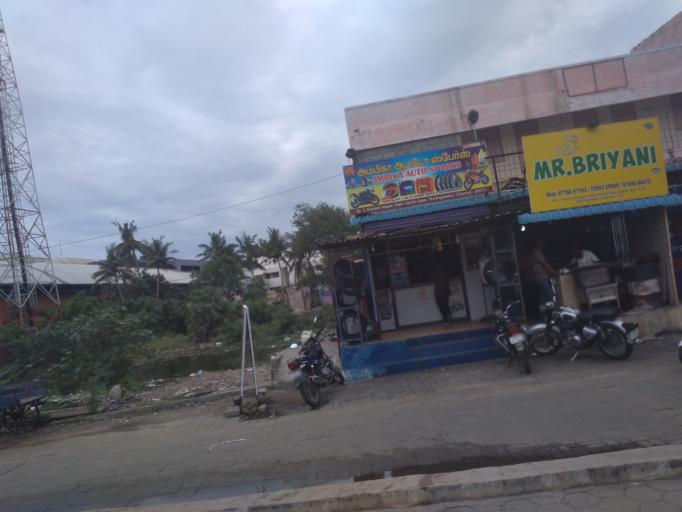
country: IN
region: Tamil Nadu
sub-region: Kancheepuram
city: Injambakkam
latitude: 12.8776
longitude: 80.2269
